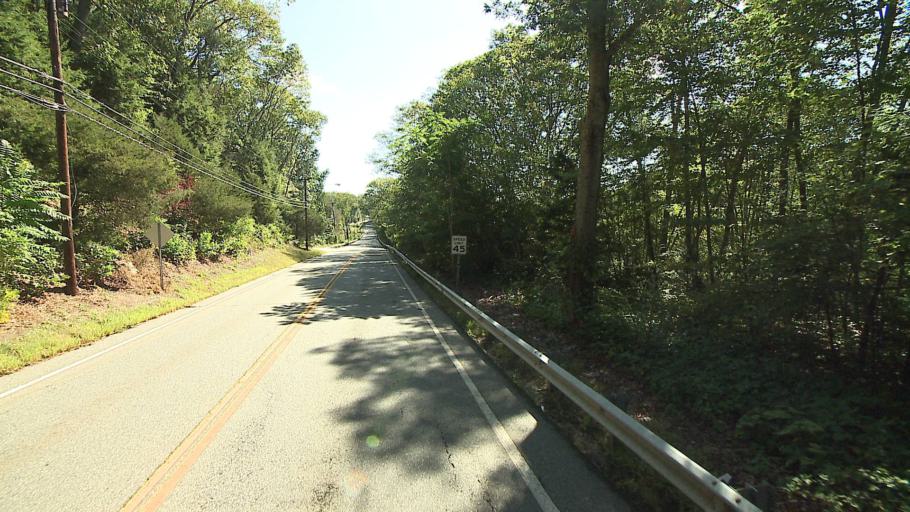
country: US
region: Connecticut
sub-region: New London County
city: Lisbon
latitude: 41.5562
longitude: -72.0303
